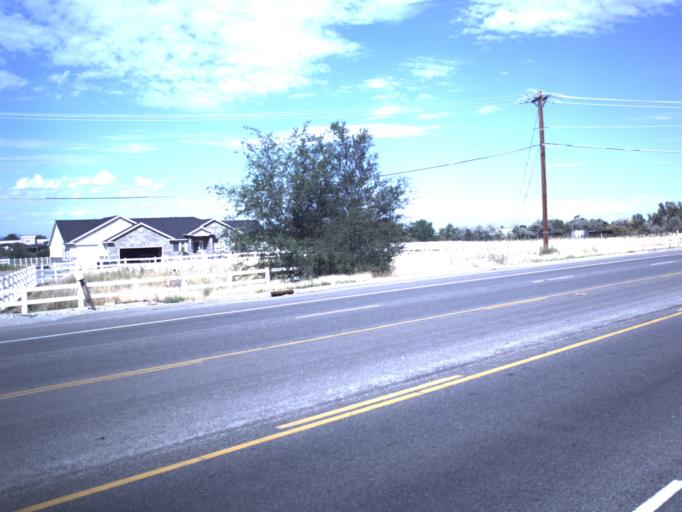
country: US
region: Utah
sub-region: Weber County
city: Harrisville
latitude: 41.2845
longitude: -111.9877
